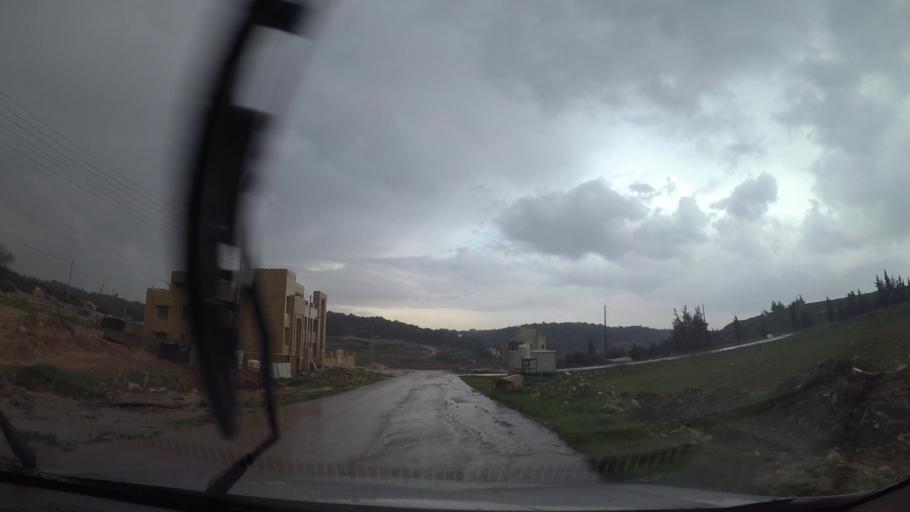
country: JO
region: Amman
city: Umm as Summaq
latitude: 31.8738
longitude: 35.8738
